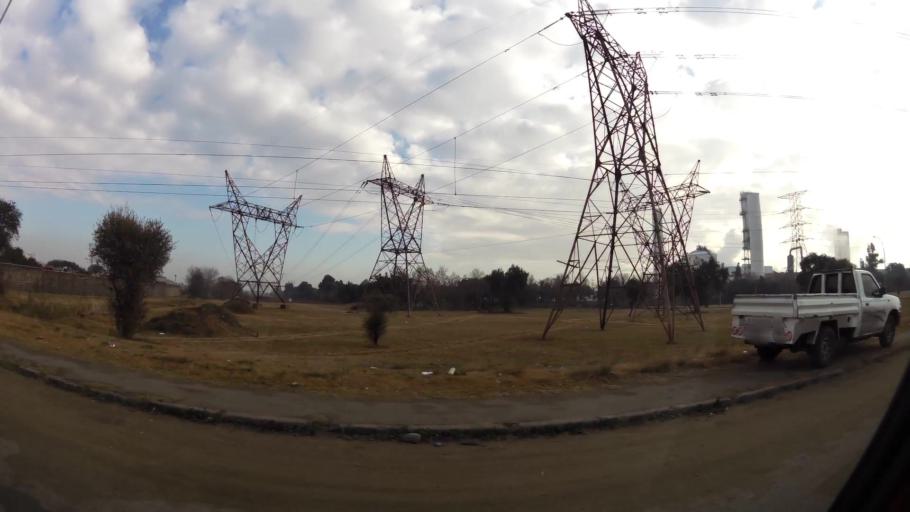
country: ZA
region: Gauteng
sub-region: Sedibeng District Municipality
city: Vanderbijlpark
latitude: -26.6734
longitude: 27.8047
